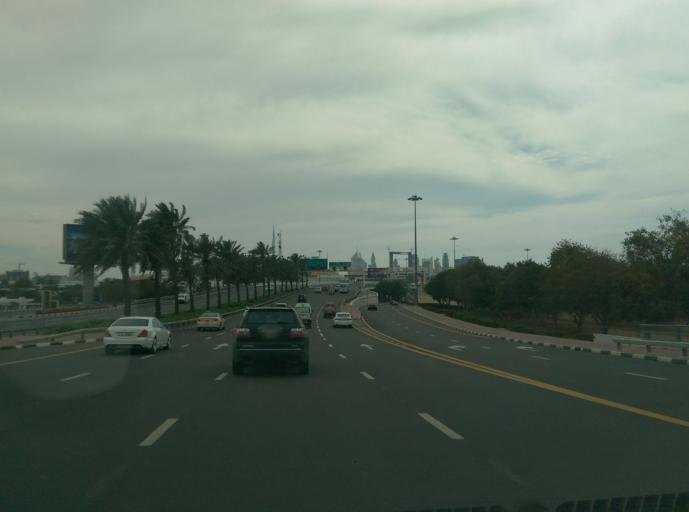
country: AE
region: Ash Shariqah
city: Sharjah
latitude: 25.2512
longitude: 55.3203
